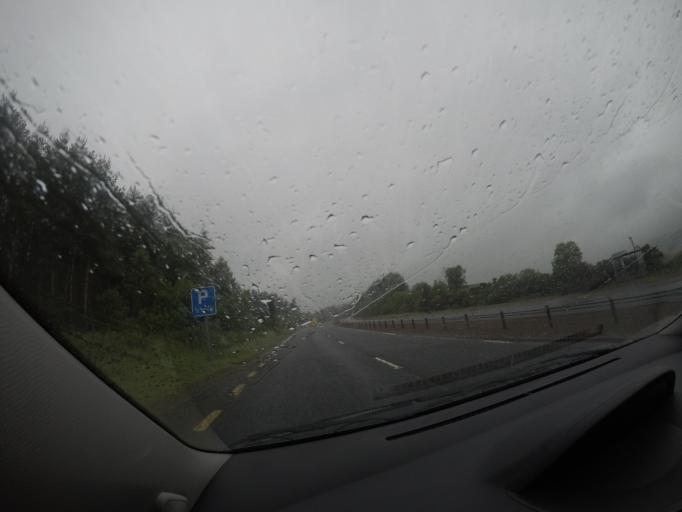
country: GB
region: Scotland
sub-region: Angus
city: Forfar
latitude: 56.5557
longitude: -2.9279
